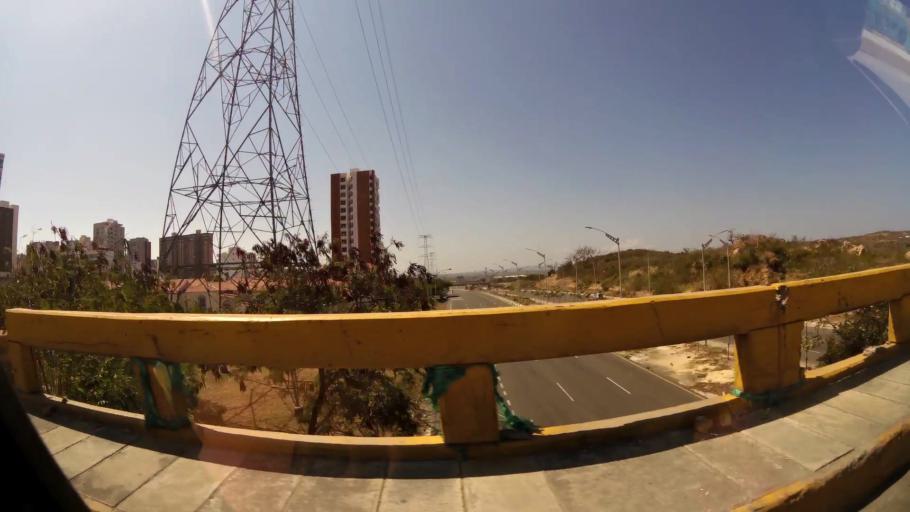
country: CO
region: Atlantico
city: Barranquilla
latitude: 11.0156
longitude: -74.8385
